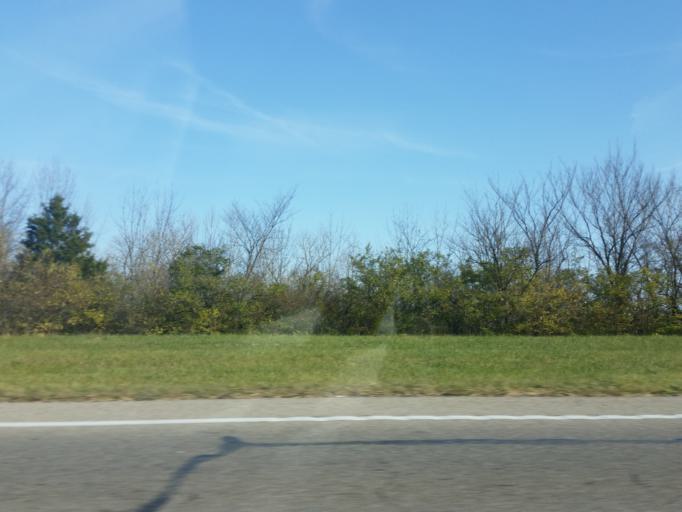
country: US
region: Ohio
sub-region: Butler County
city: Ross
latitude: 39.3525
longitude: -84.6376
